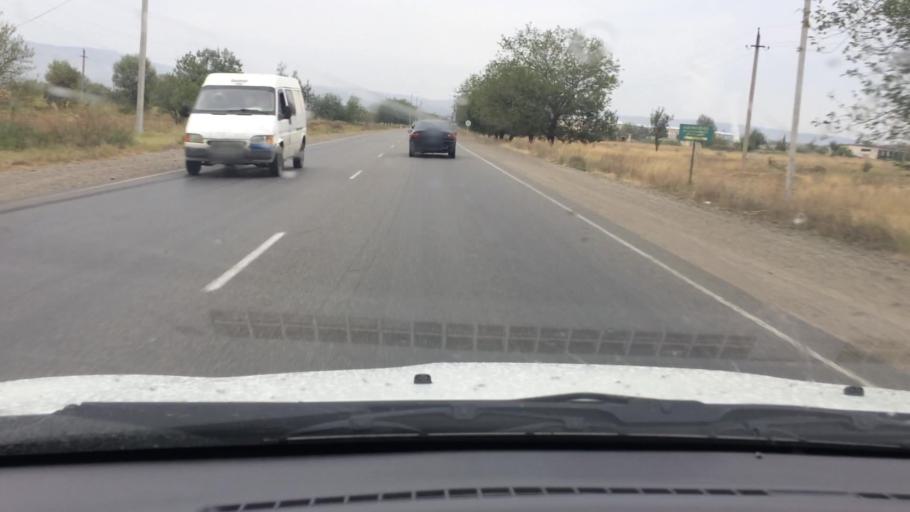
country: GE
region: Kvemo Kartli
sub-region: Marneuli
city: Marneuli
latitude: 41.5674
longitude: 44.7754
